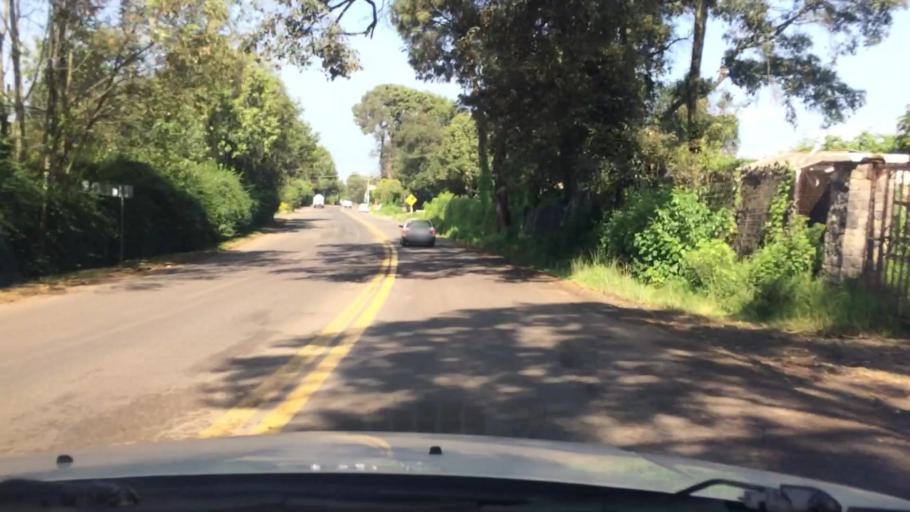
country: MX
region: Mexico
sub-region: Valle de Bravo
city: Casas Viejas
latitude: 19.1592
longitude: -100.0987
